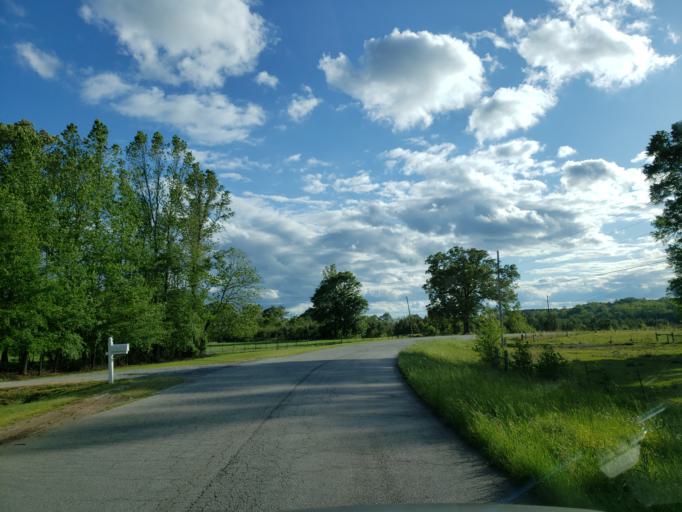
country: US
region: Georgia
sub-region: Haralson County
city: Tallapoosa
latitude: 33.7848
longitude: -85.3025
